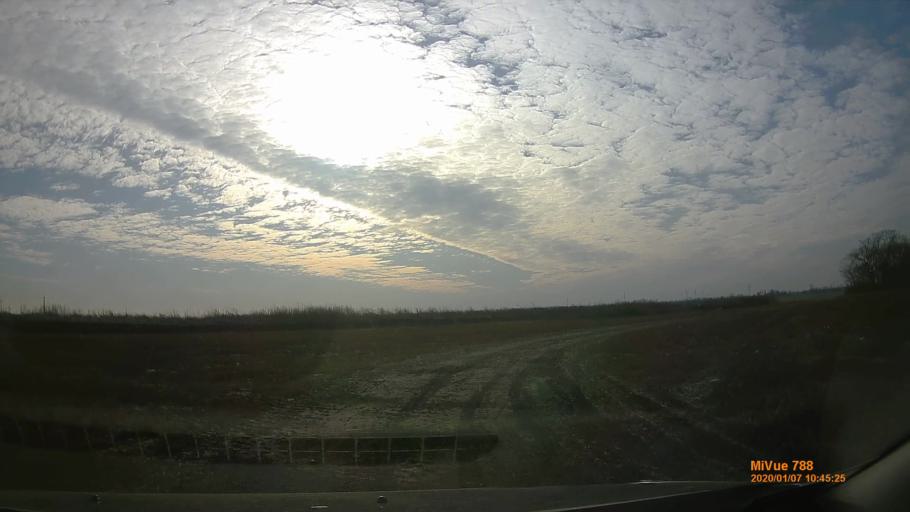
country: HU
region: Gyor-Moson-Sopron
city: Rajka
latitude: 47.9178
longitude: 17.1914
